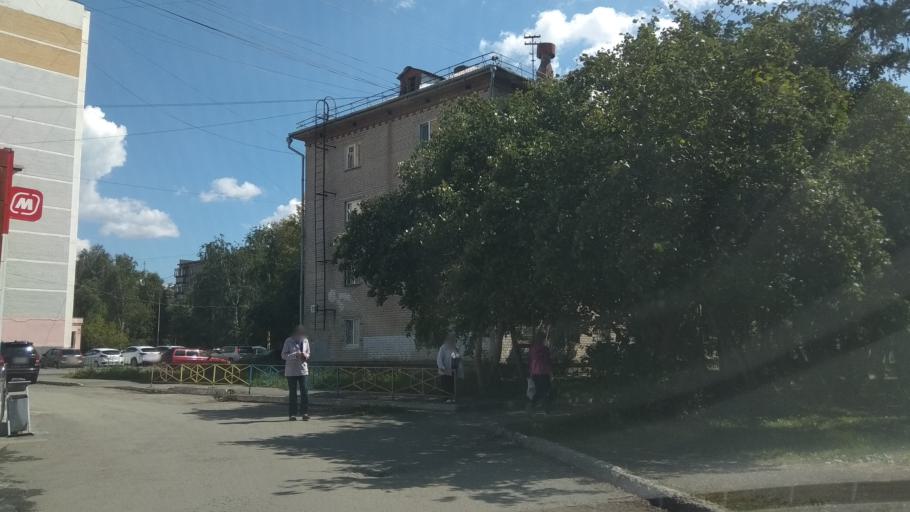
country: RU
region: Sverdlovsk
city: Yekaterinburg
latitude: 56.8340
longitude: 60.6899
